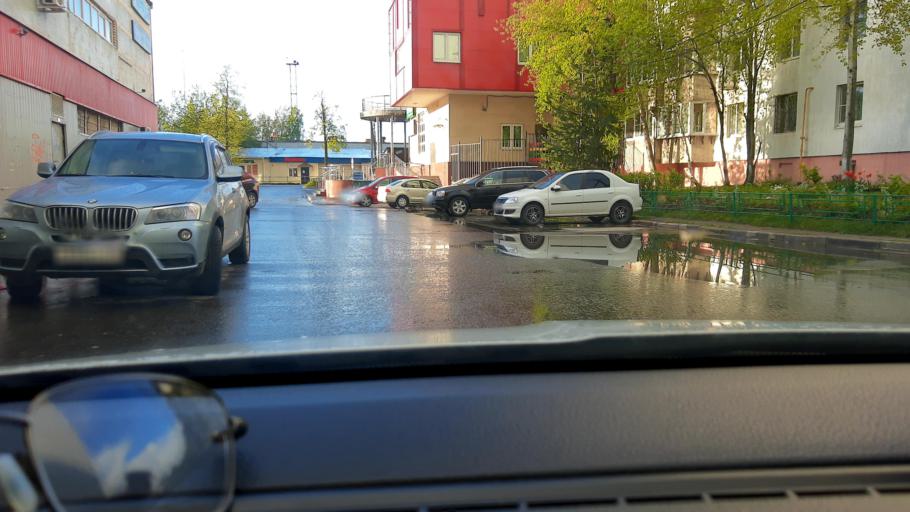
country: RU
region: Moskovskaya
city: Nakhabino
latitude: 55.8397
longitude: 37.1764
